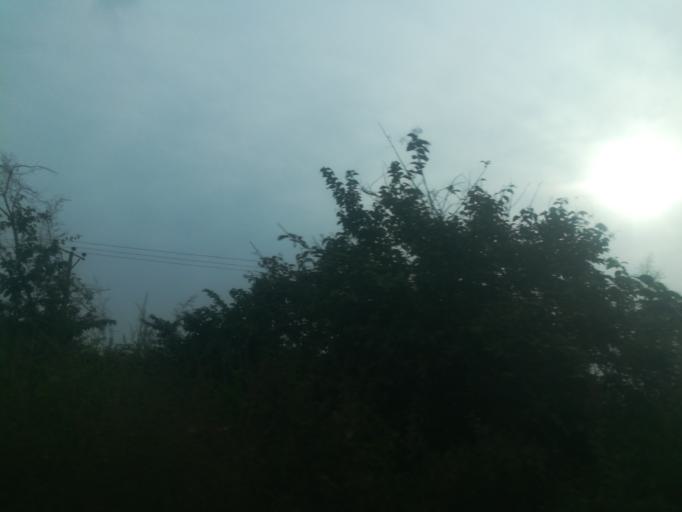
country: NG
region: Ogun
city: Ayetoro
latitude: 7.2374
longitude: 3.1299
